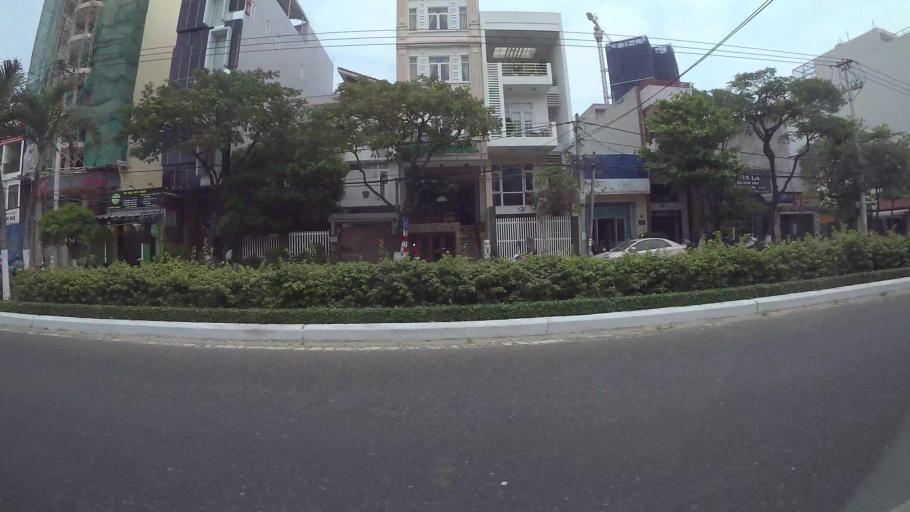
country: VN
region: Da Nang
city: Da Nang
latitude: 16.0855
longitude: 108.2193
